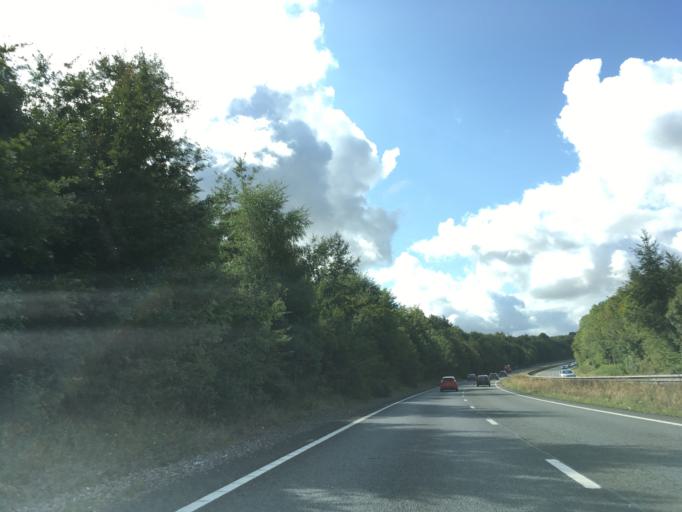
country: GB
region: England
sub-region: Hampshire
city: Highclere
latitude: 51.3397
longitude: -1.3405
